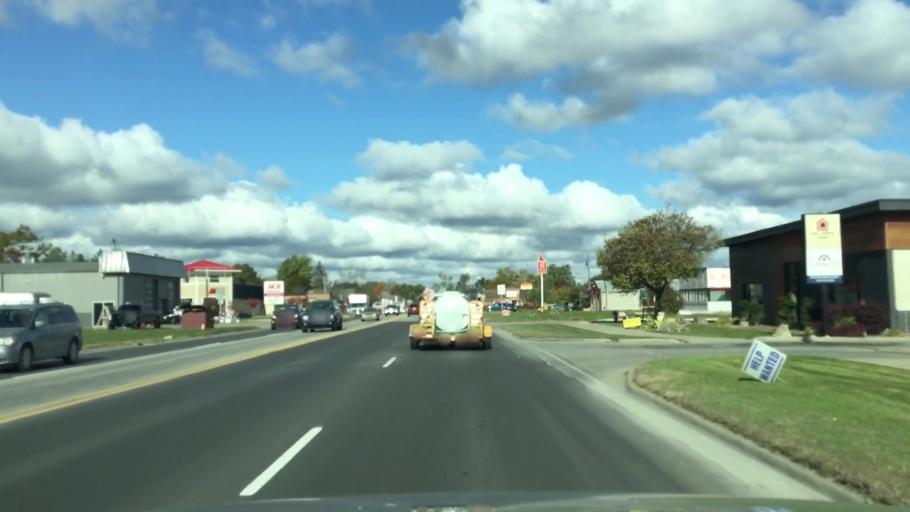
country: US
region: Michigan
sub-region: Oakland County
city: Oxford
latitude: 42.8158
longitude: -83.2567
